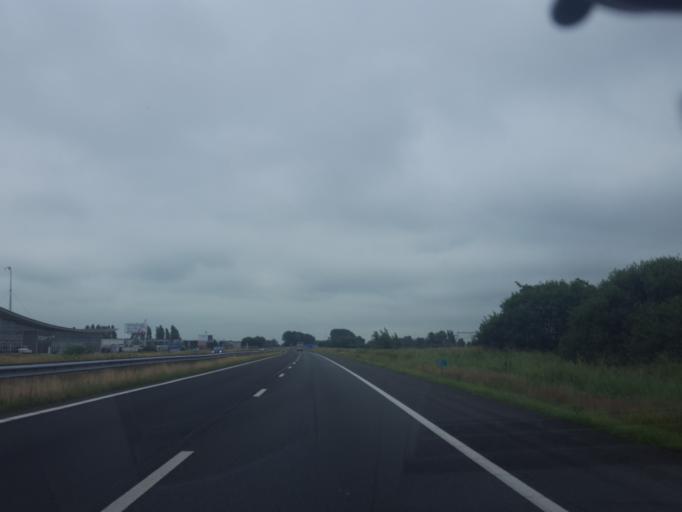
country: NL
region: Friesland
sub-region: Gemeente Boarnsterhim
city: Grou
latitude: 53.1005
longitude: 5.8178
